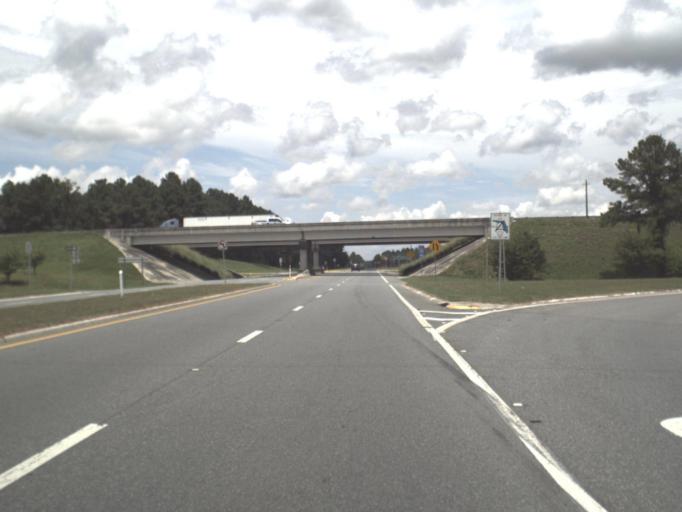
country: US
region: Florida
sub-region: Suwannee County
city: Live Oak
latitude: 30.3295
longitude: -82.9634
